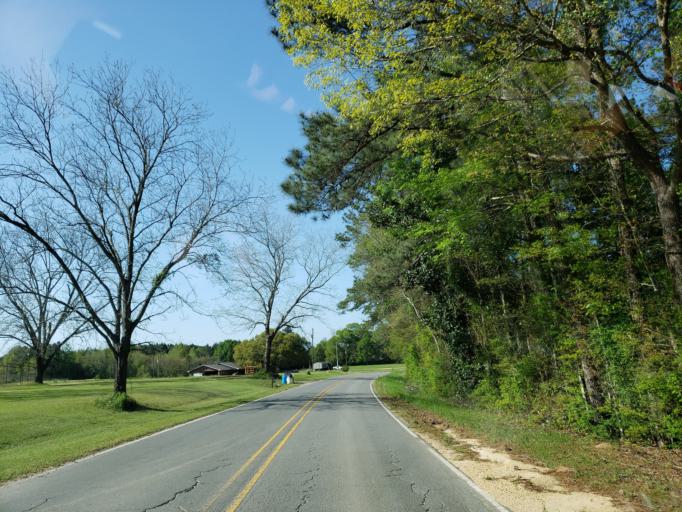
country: US
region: Mississippi
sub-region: Forrest County
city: Rawls Springs
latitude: 31.5005
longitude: -89.3598
